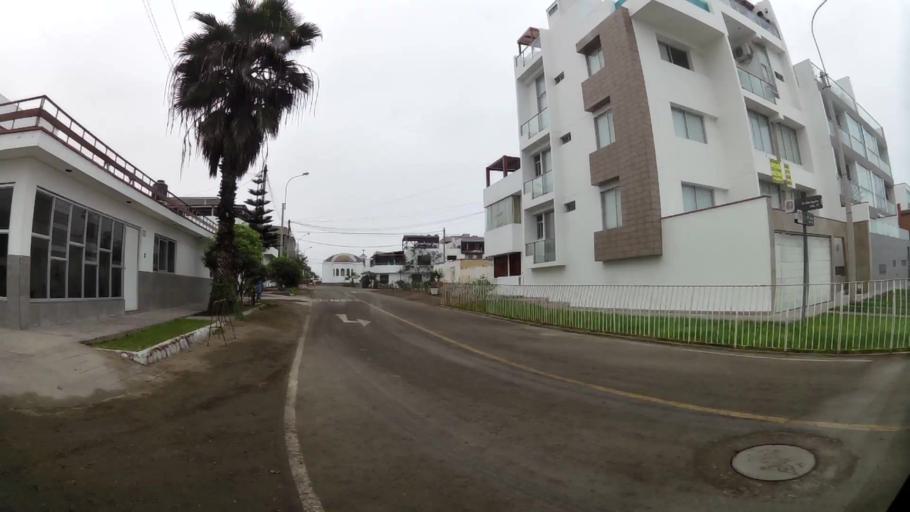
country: PE
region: Lima
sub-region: Lima
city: Punta Hermosa
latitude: -12.3371
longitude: -76.8277
